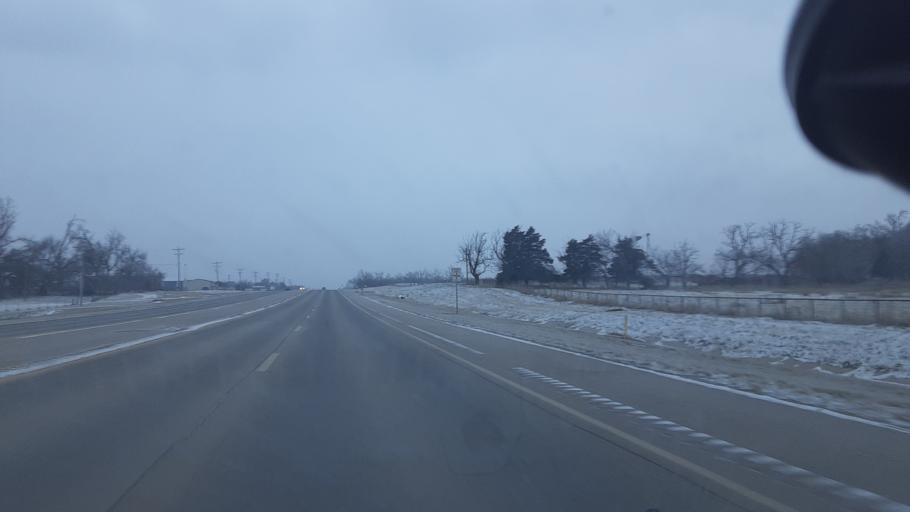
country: US
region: Oklahoma
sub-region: Payne County
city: Perkins
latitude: 35.9855
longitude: -97.0627
